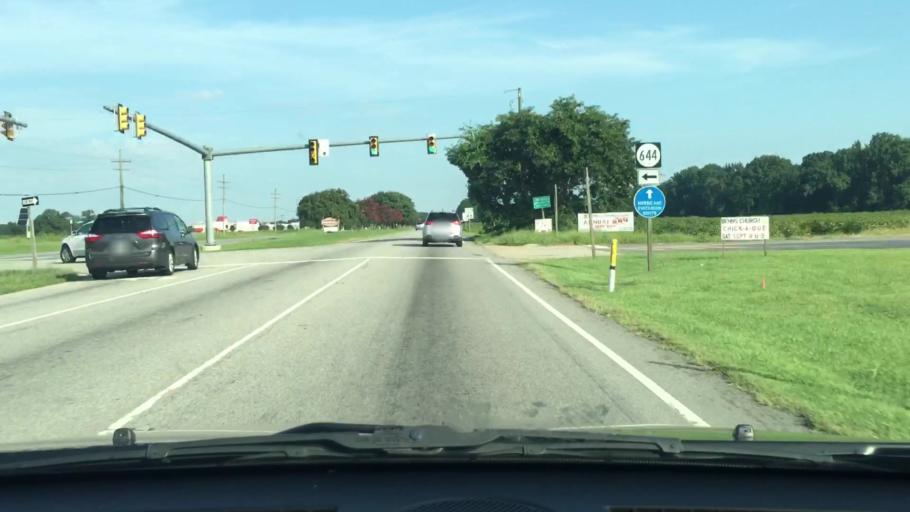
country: US
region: Virginia
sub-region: Isle of Wight County
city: Carrollton
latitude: 36.9494
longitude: -76.5963
